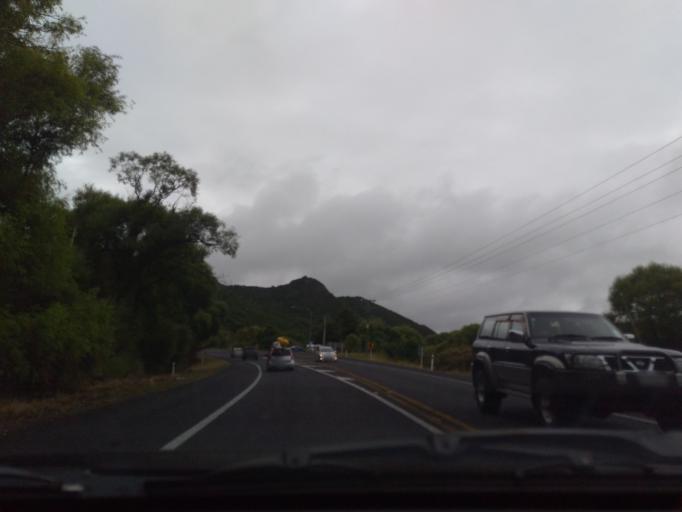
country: NZ
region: Auckland
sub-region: Auckland
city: Wellsford
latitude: -36.1236
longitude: 174.4344
